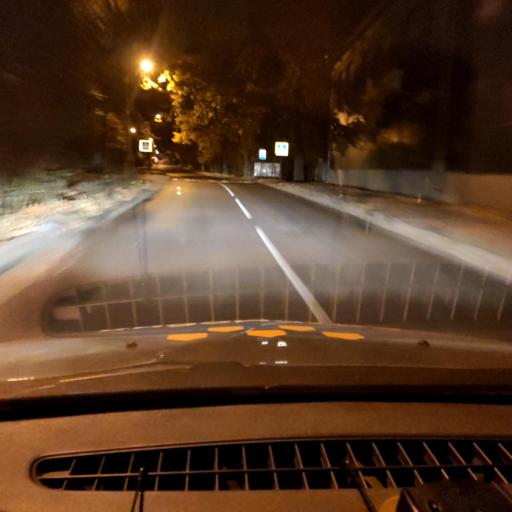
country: RU
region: Voronezj
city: Voronezh
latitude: 51.7232
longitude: 39.2211
